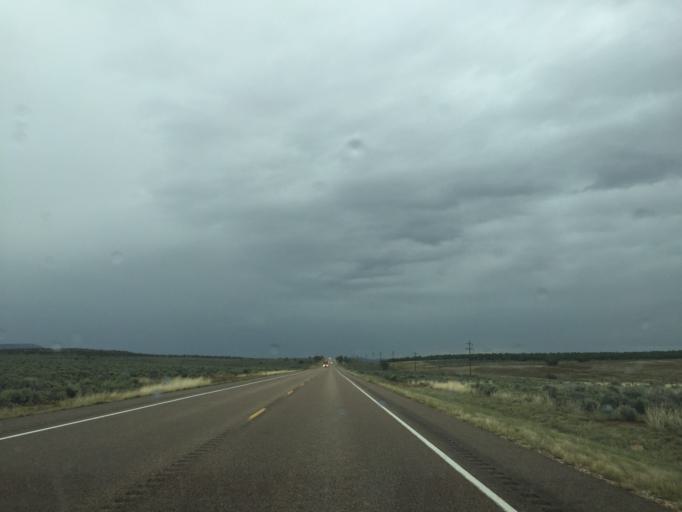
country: US
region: Utah
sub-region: Kane County
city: Kanab
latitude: 37.1372
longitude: -112.0814
